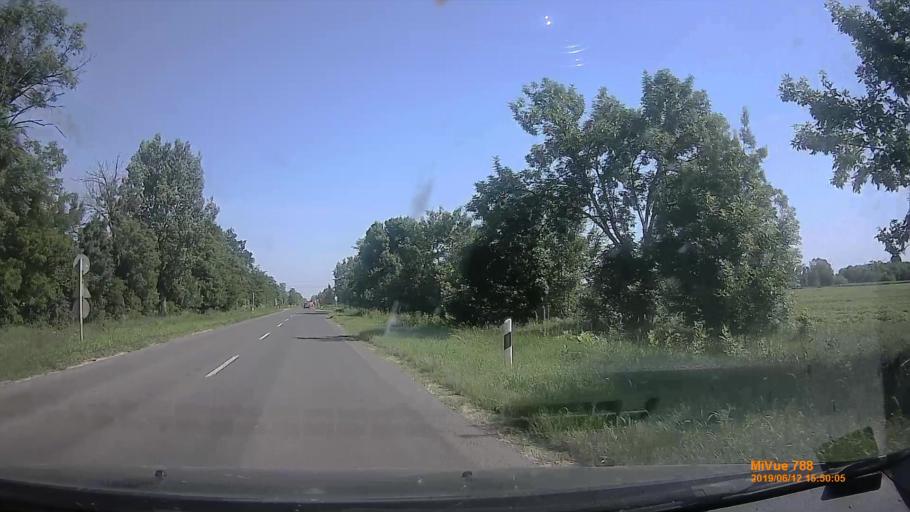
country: HU
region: Csongrad
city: Apatfalva
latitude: 46.1896
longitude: 20.5630
